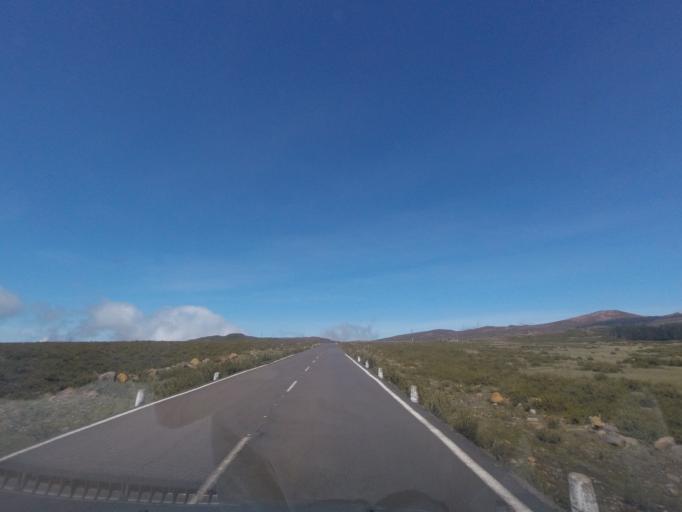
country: PT
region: Madeira
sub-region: Calheta
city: Arco da Calheta
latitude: 32.7511
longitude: -17.0986
